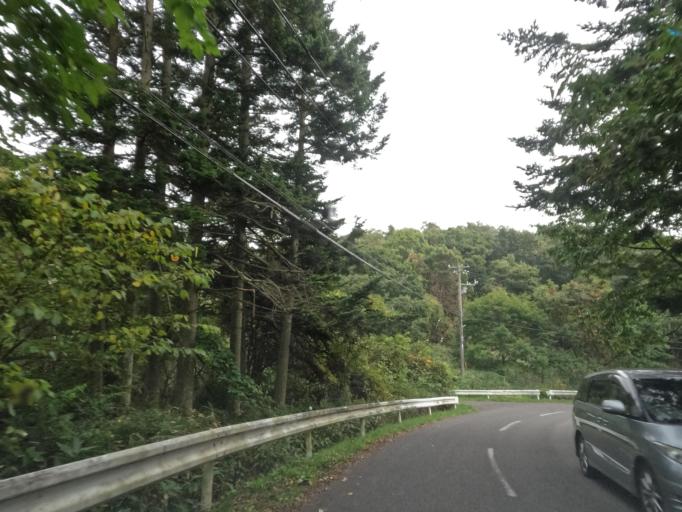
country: JP
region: Hokkaido
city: Date
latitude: 42.4027
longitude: 140.9253
